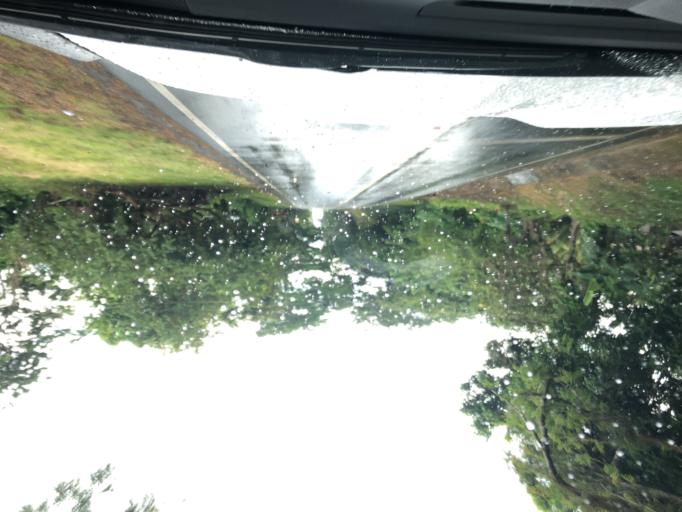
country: NI
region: Chontales
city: Villa Sandino
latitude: 12.0198
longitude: -84.9522
